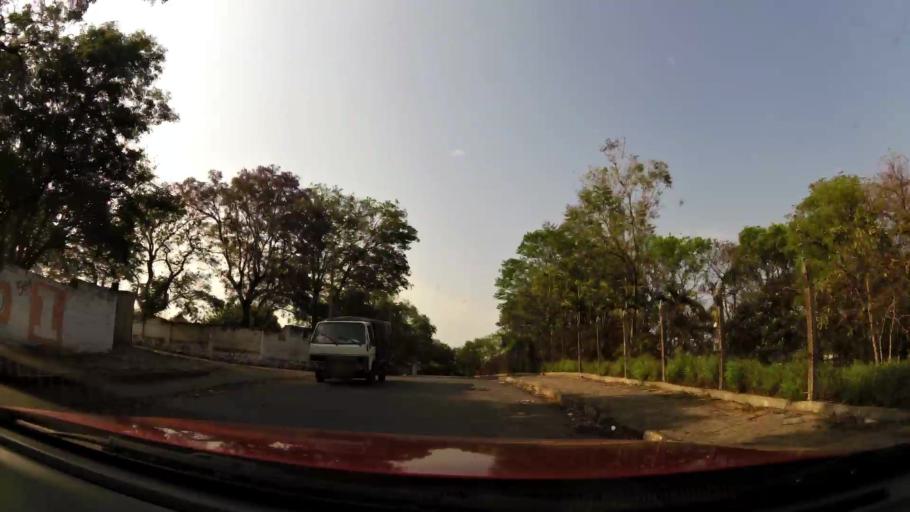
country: PY
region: Presidente Hayes
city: Nanawa
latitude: -25.2835
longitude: -57.6645
